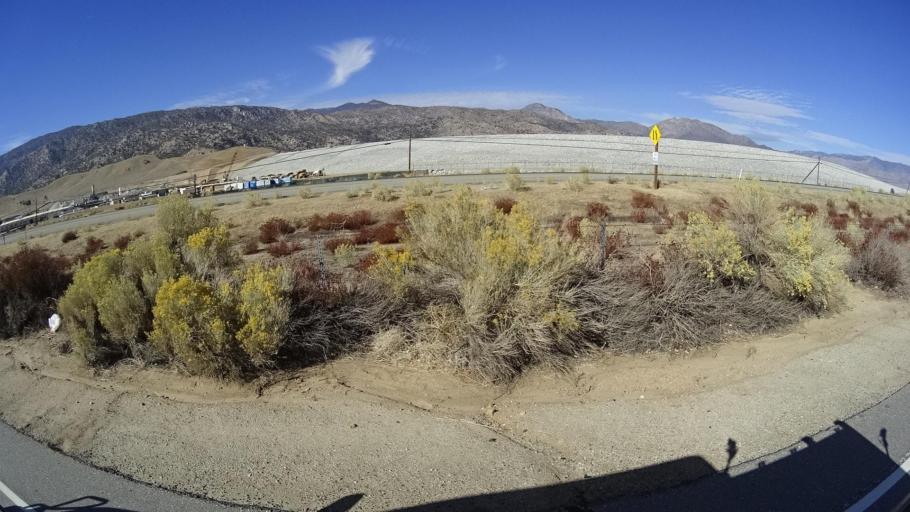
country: US
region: California
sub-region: Kern County
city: Lake Isabella
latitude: 35.6451
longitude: -118.4643
